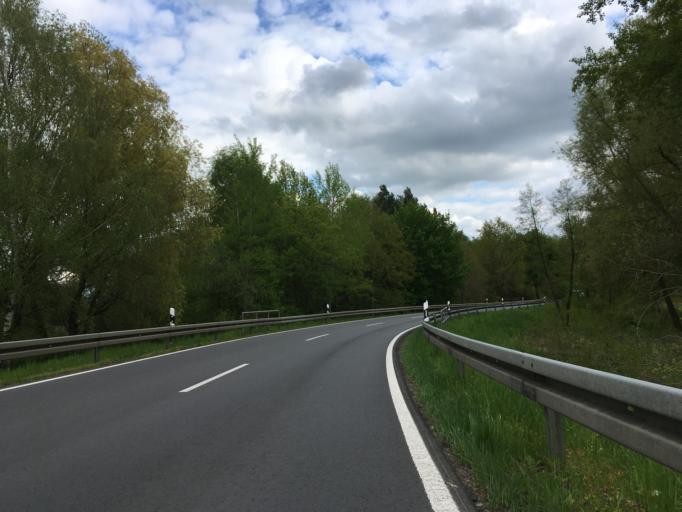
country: DE
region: Brandenburg
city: Bernau bei Berlin
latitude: 52.6443
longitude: 13.6103
